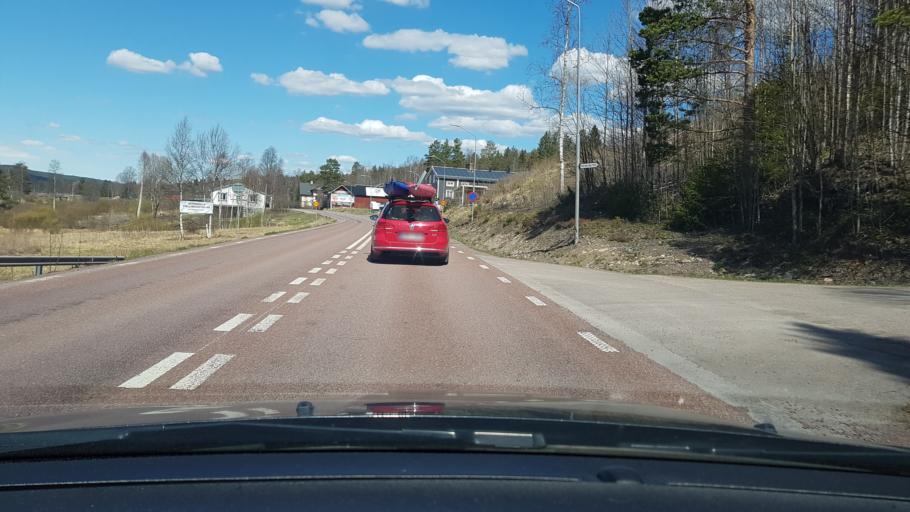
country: SE
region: Dalarna
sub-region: Malung-Saelens kommun
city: Malung
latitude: 61.0875
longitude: 13.3219
